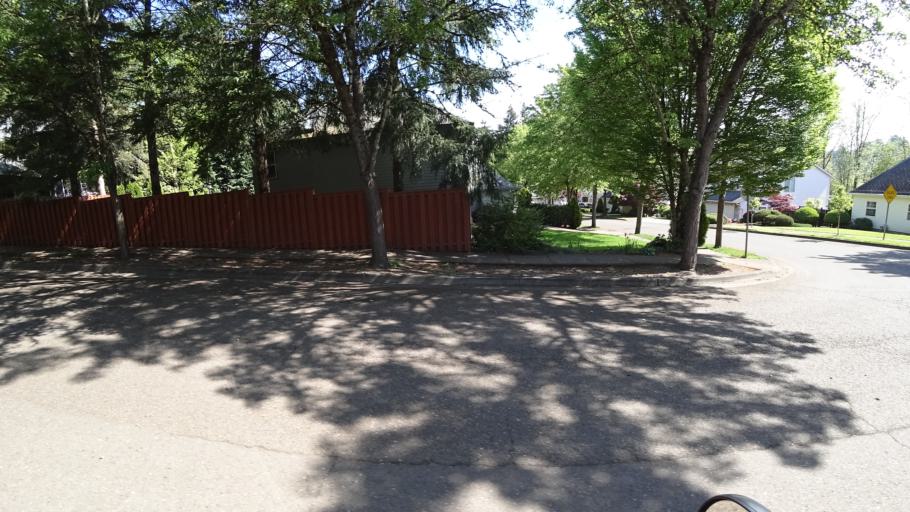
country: US
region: Oregon
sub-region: Washington County
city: Beaverton
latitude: 45.4559
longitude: -122.8391
